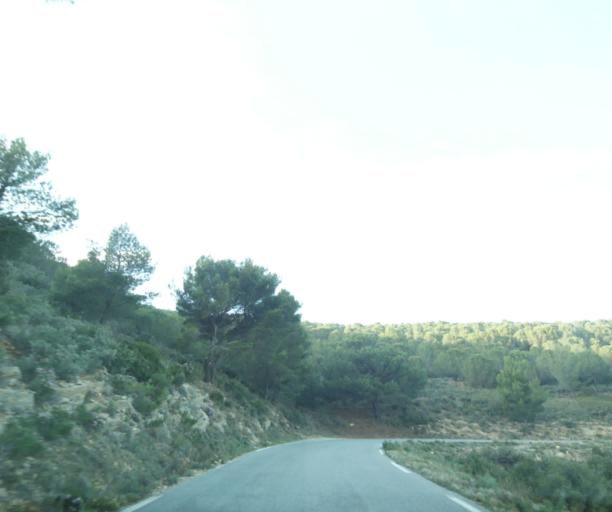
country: FR
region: Provence-Alpes-Cote d'Azur
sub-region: Departement des Bouches-du-Rhone
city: Cassis
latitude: 43.1929
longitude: 5.5555
